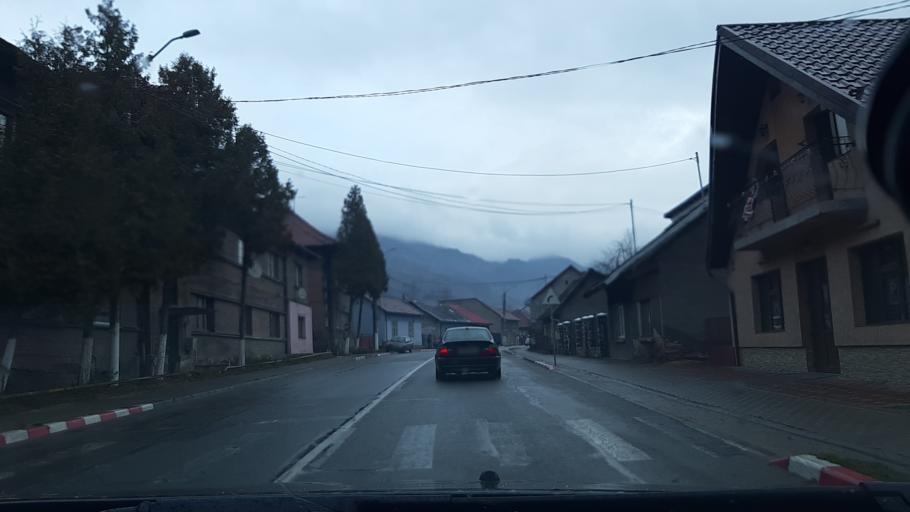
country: RO
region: Hunedoara
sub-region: Municipiul Petrosani
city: Petrosani
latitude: 45.4402
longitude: 23.3699
